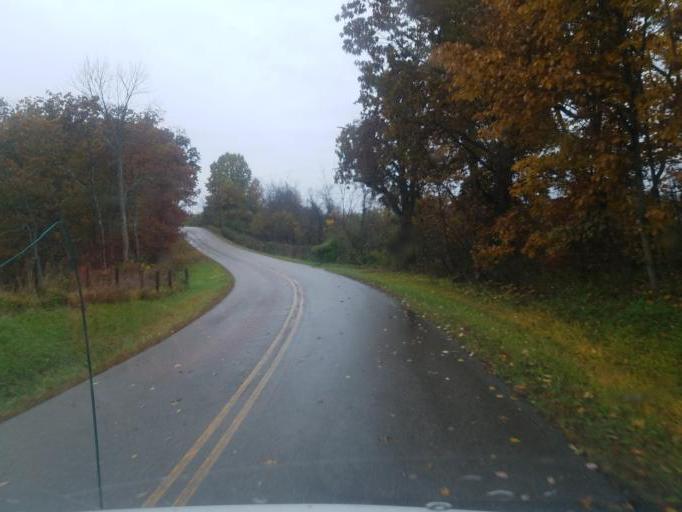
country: US
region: Ohio
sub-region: Washington County
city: Beverly
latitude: 39.4572
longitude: -81.6164
